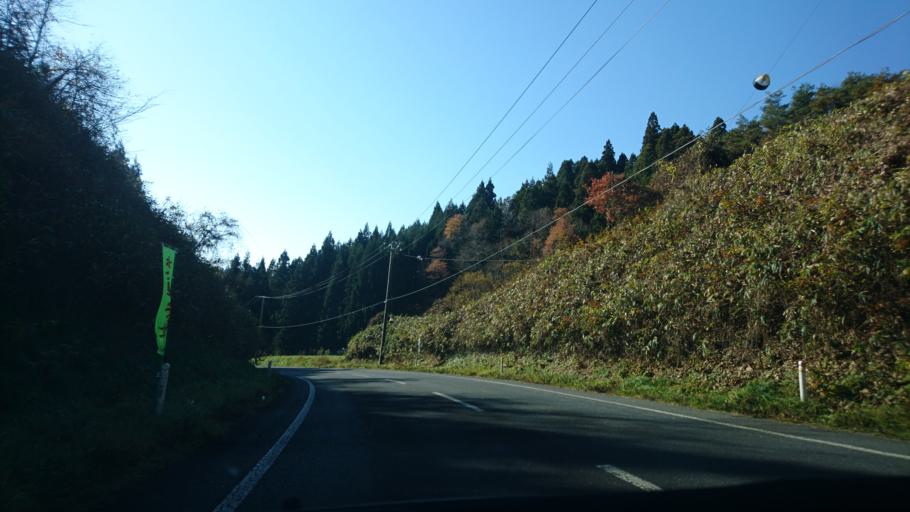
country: JP
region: Iwate
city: Ichinoseki
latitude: 38.9031
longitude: 141.4100
